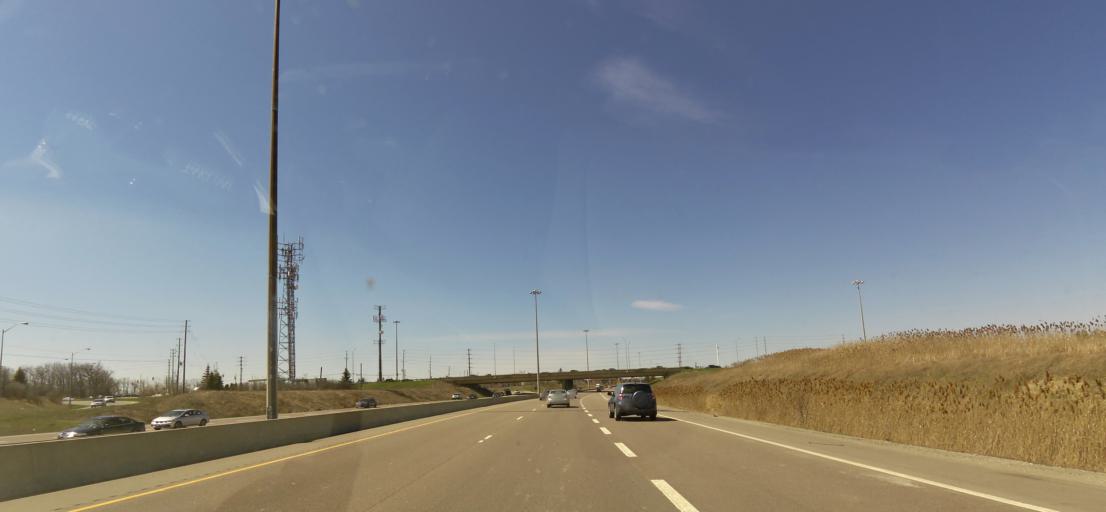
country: CA
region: Ontario
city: Brampton
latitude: 43.7241
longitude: -79.7630
